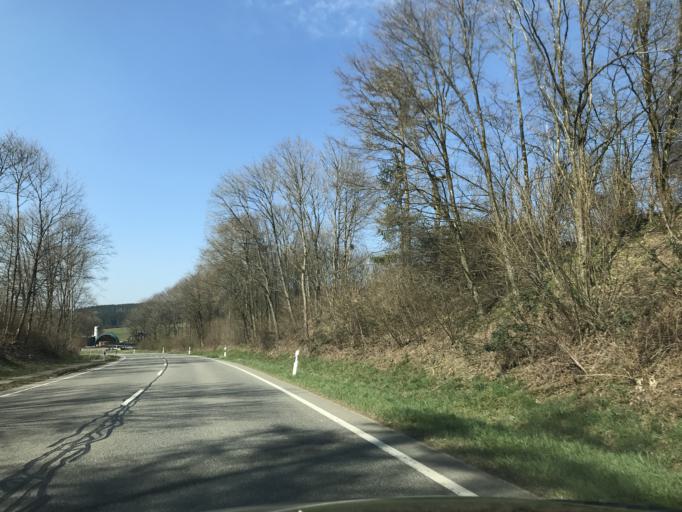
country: DE
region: Rheinland-Pfalz
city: Neuhutten
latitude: 49.6037
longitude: 7.0224
